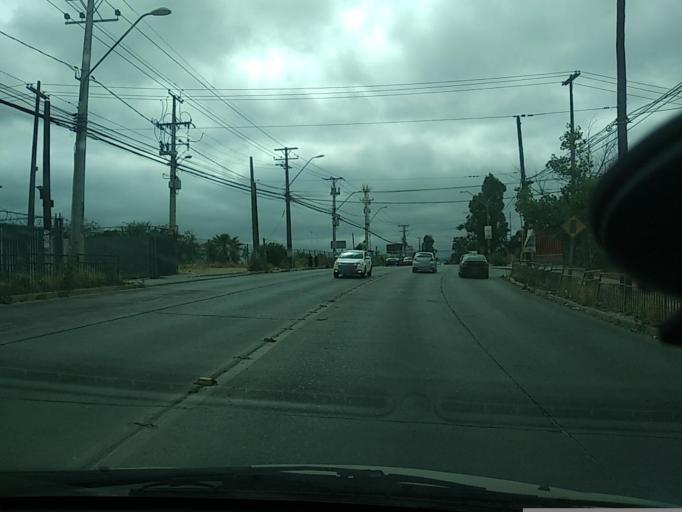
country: CL
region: Valparaiso
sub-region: Provincia de Marga Marga
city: Villa Alemana
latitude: -33.0458
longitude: -71.4002
